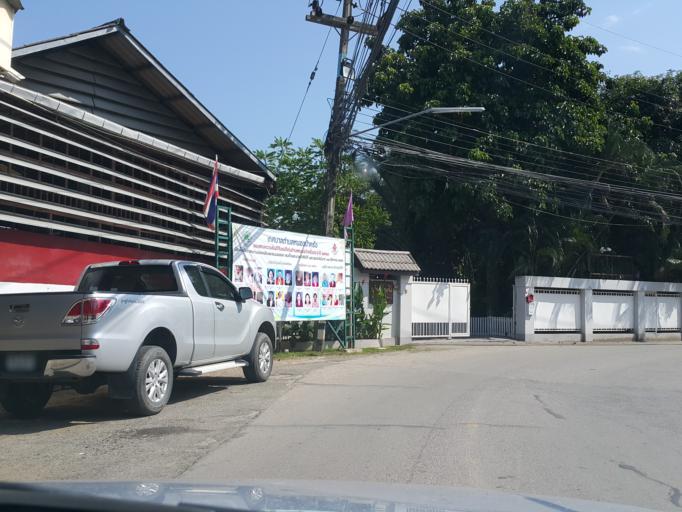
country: TH
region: Chiang Mai
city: Chiang Mai
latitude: 18.7884
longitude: 99.0298
